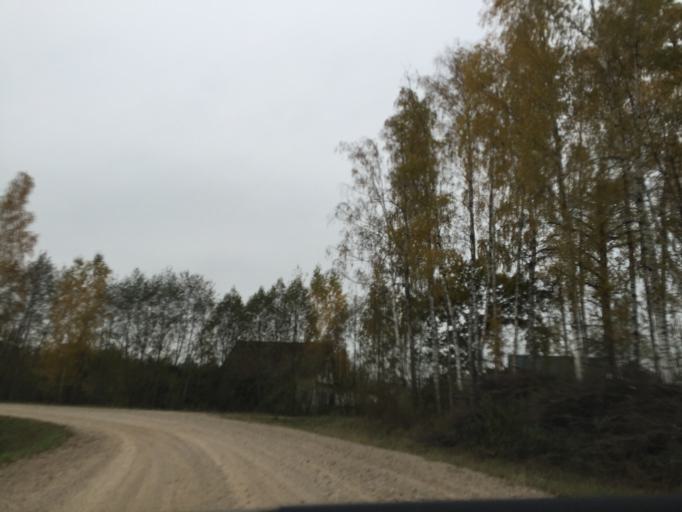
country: LV
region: Jelgava
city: Jelgava
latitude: 56.6362
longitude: 23.6251
